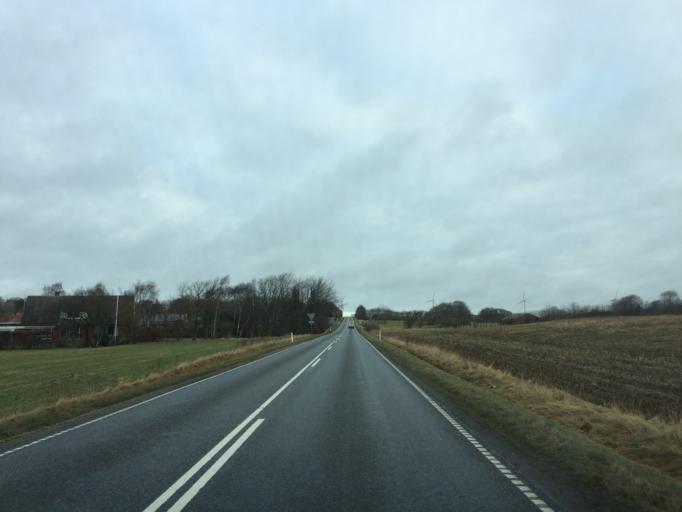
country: DK
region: Central Jutland
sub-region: Struer Kommune
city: Struer
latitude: 56.4158
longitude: 8.4900
